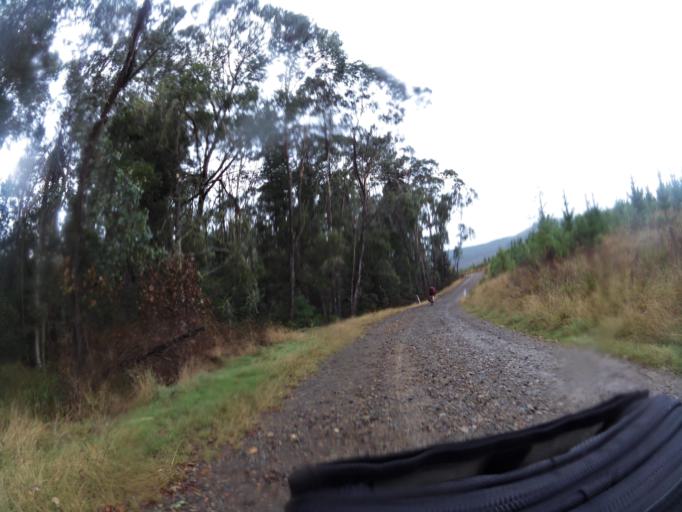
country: AU
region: New South Wales
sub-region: Greater Hume Shire
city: Holbrook
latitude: -36.2131
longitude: 147.5691
